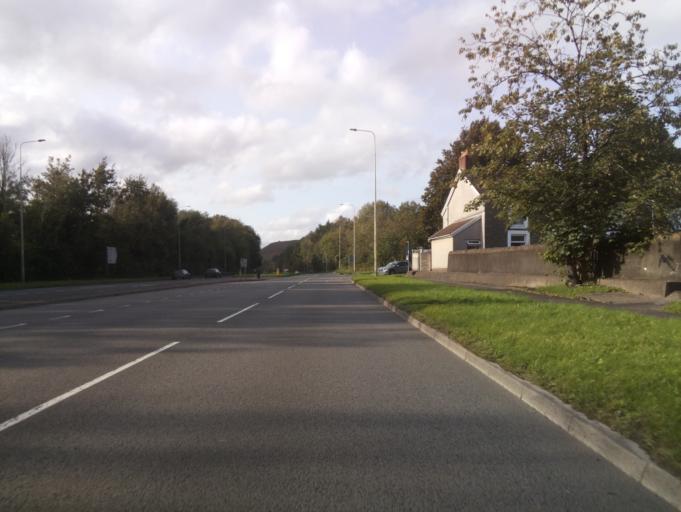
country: GB
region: Wales
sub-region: Rhondda Cynon Taf
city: Llantrisant
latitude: 51.5272
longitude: -3.3661
